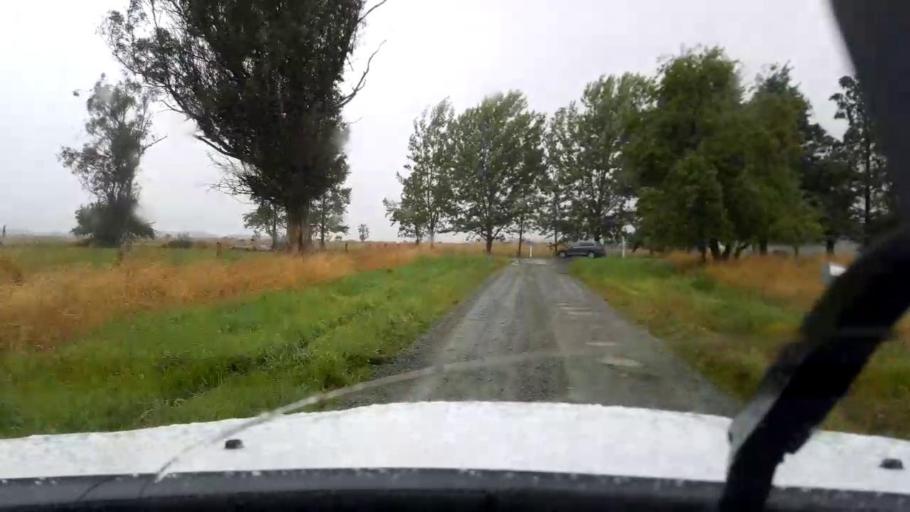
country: NZ
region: Canterbury
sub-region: Timaru District
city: Pleasant Point
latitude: -44.2028
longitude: 171.0896
